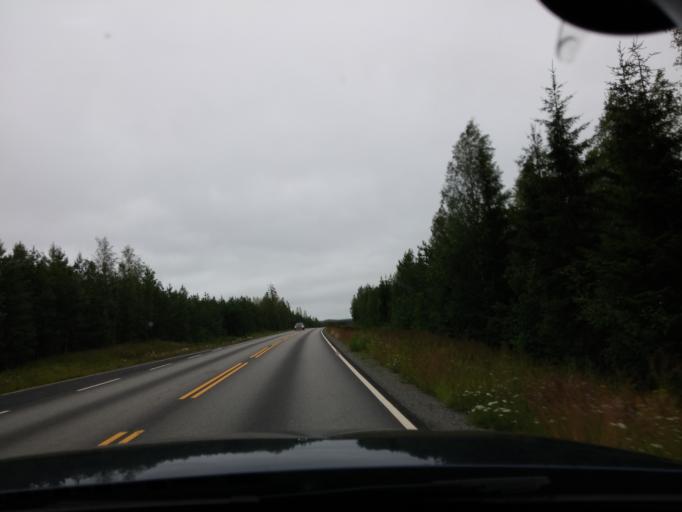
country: FI
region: Central Finland
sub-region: Saarijaervi-Viitasaari
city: Saarijaervi
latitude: 62.6795
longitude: 25.1867
